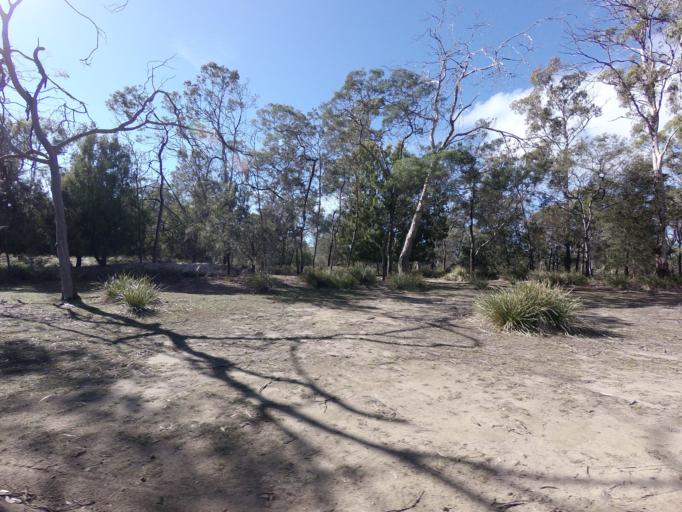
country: AU
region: Tasmania
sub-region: Clarence
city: Sandford
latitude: -42.9575
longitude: 147.7044
